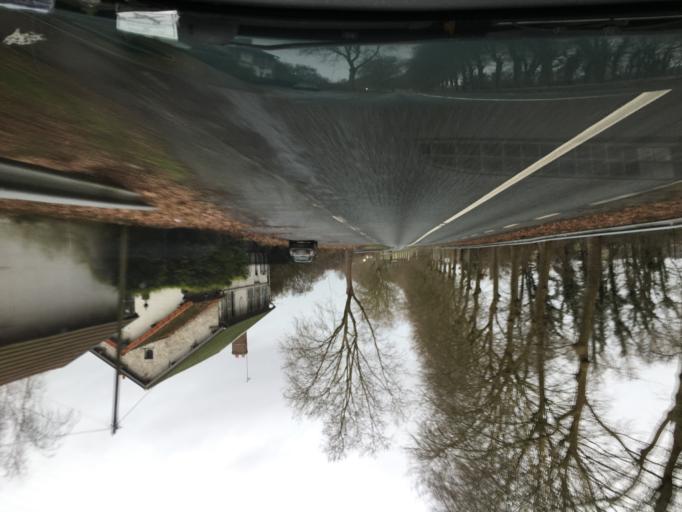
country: FR
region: Picardie
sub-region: Departement de l'Oise
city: La Chapelle-en-Serval
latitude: 49.1432
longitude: 2.5407
